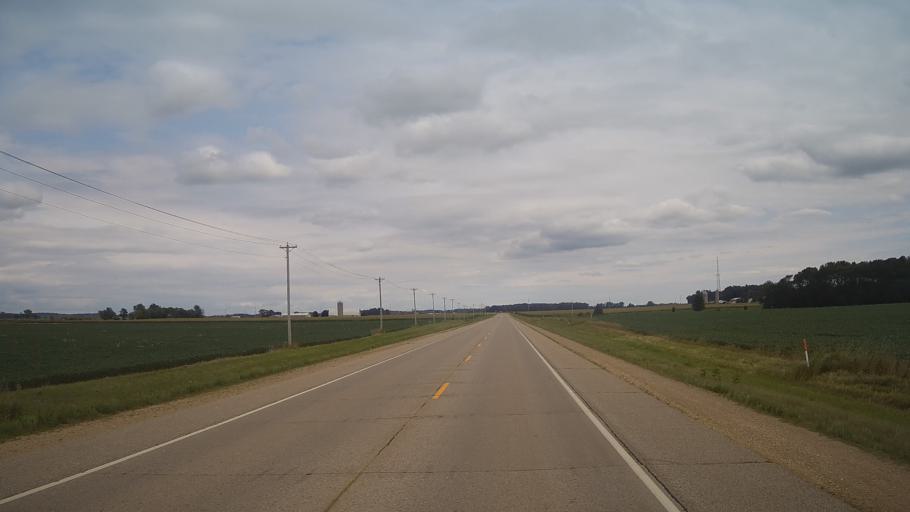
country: US
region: Wisconsin
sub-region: Waushara County
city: Redgranite
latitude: 44.0375
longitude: -89.0591
